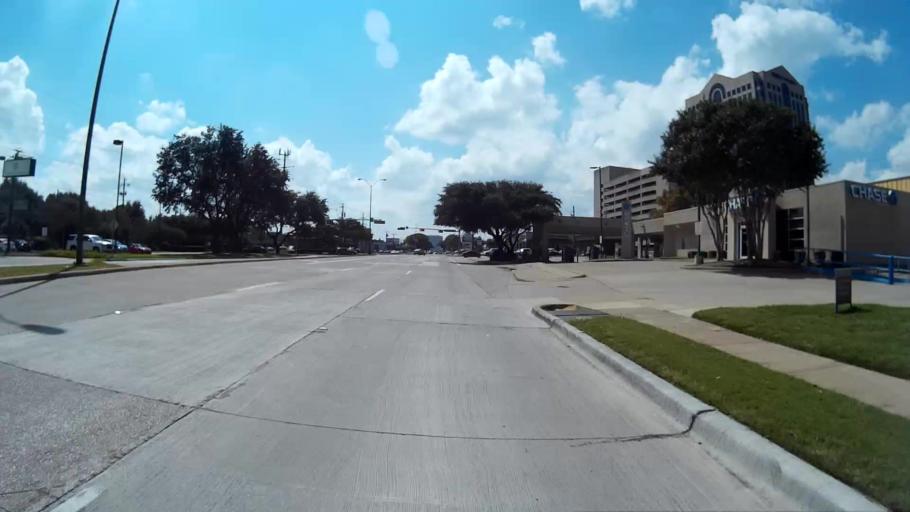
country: US
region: Texas
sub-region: Dallas County
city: University Park
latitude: 32.8618
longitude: -96.7677
